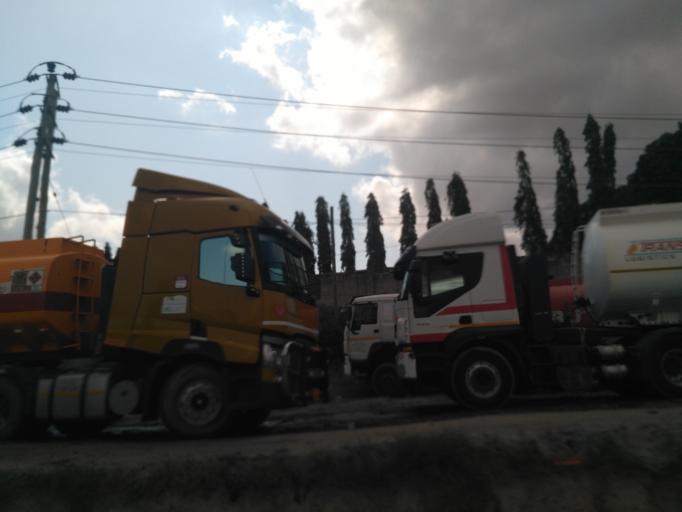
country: TZ
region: Dar es Salaam
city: Dar es Salaam
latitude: -6.8469
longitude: 39.2922
